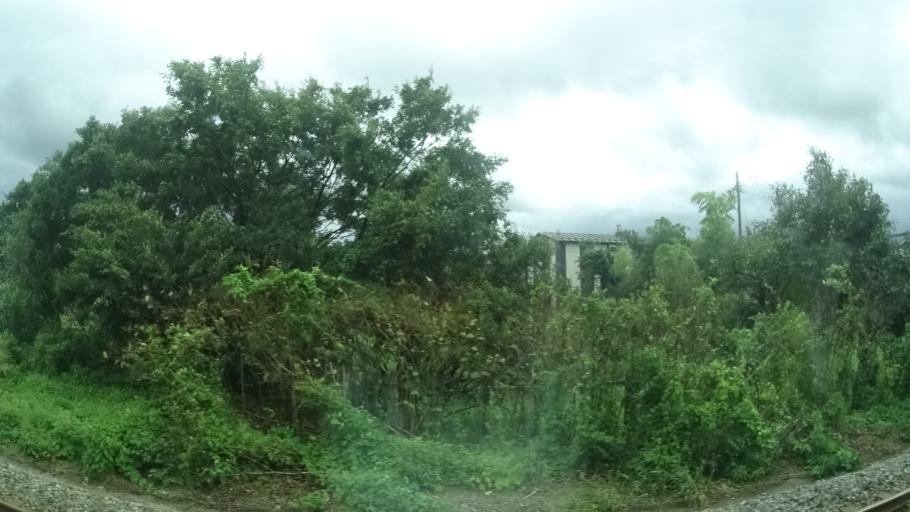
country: JP
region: Niigata
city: Murakami
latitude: 38.1173
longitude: 139.4442
